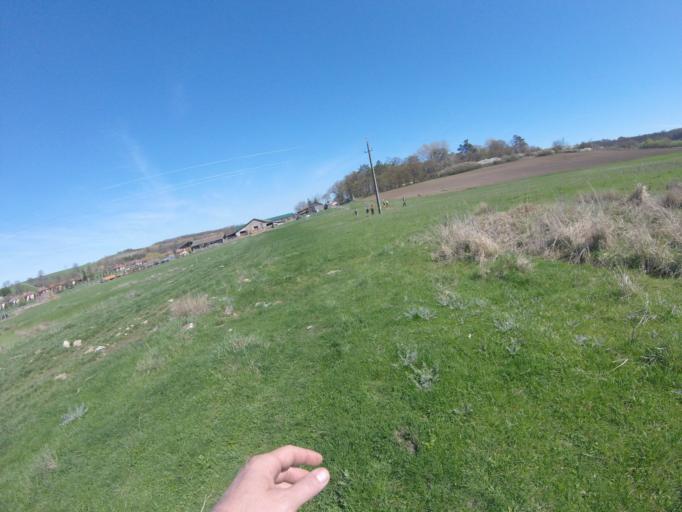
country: HU
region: Borsod-Abauj-Zemplen
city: Szendro
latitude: 48.4149
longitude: 20.7745
